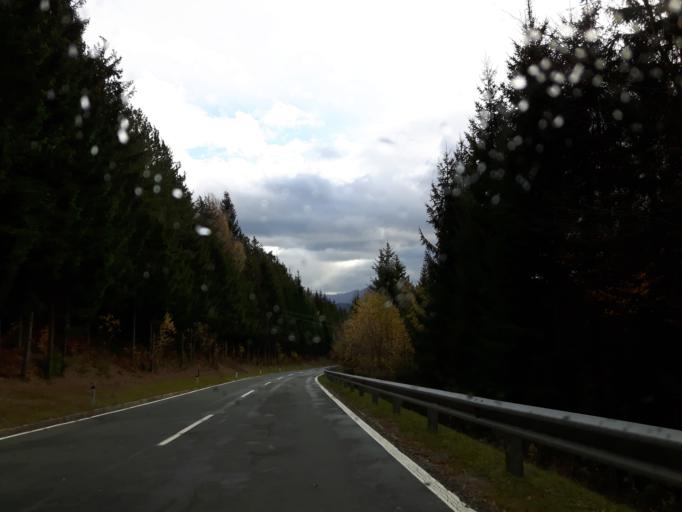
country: AT
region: Carinthia
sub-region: Politischer Bezirk Wolfsberg
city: Lavamund
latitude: 46.6524
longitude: 14.9824
